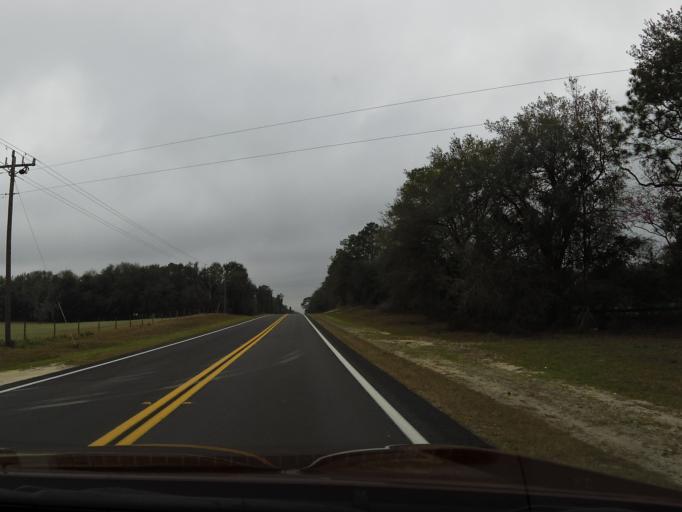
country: US
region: Florida
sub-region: Gilchrist County
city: Trenton
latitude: 29.7962
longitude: -82.8433
